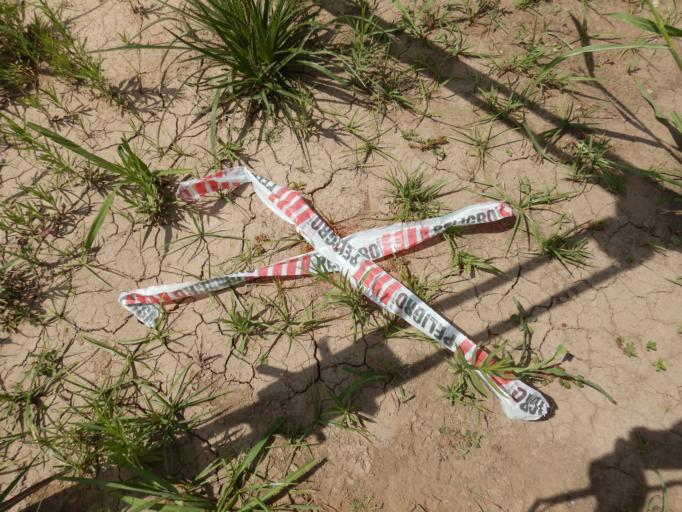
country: AR
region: Santa Fe
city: Canada de Gomez
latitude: -32.8053
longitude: -61.4090
